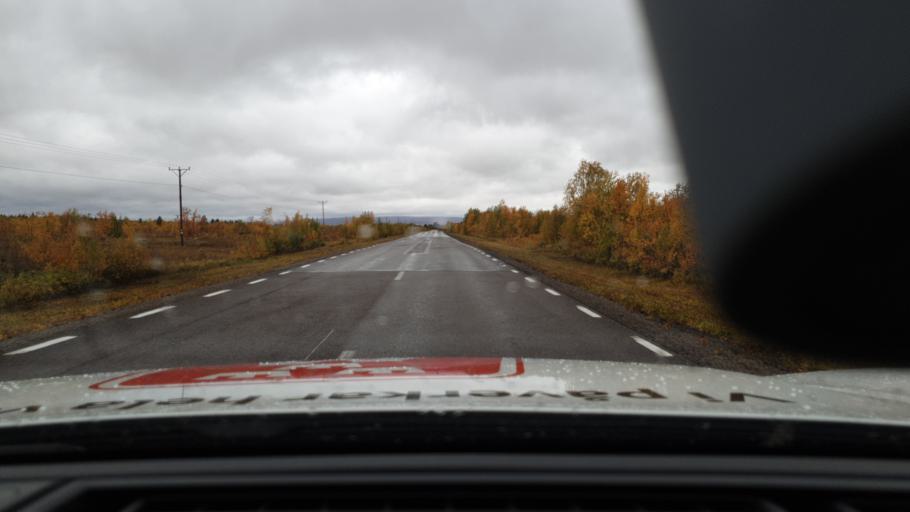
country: SE
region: Norrbotten
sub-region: Kiruna Kommun
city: Kiruna
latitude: 67.7679
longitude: 20.1585
